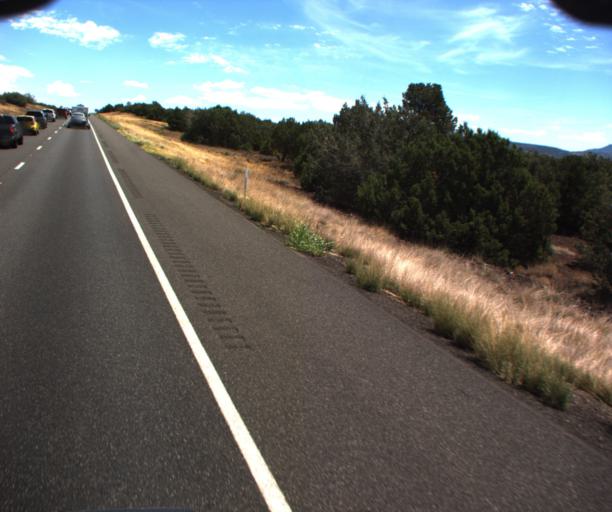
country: US
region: Arizona
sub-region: Yavapai County
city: Village of Oak Creek (Big Park)
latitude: 34.7409
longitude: -111.6898
